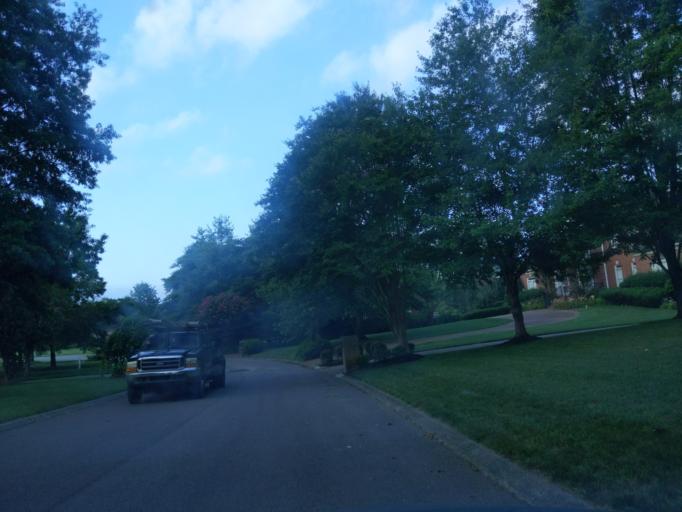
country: US
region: Tennessee
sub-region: Williamson County
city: Brentwood Estates
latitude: 36.0119
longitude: -86.7684
